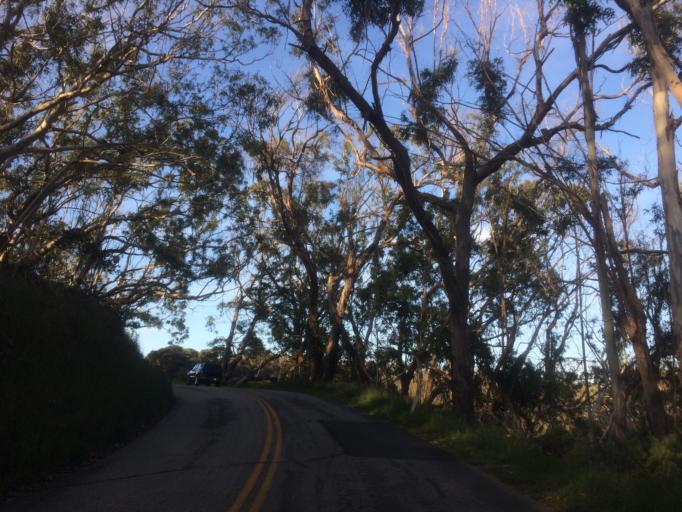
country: US
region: California
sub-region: San Luis Obispo County
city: Los Osos
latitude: 35.2925
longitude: -120.8727
